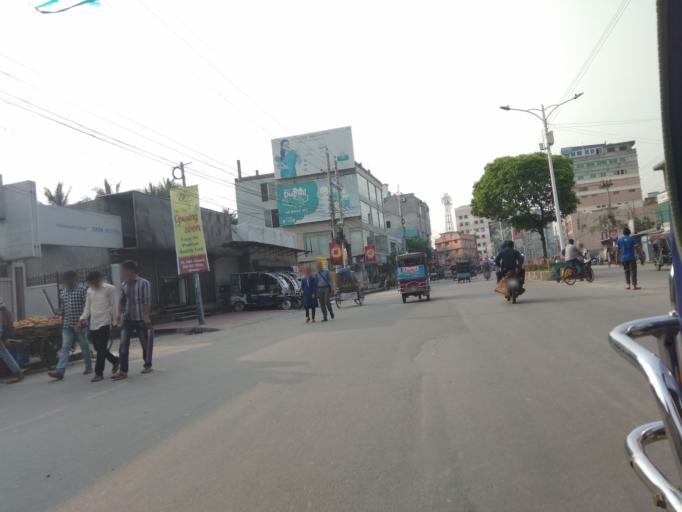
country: BD
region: Khulna
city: Khulna
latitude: 22.8143
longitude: 89.5554
